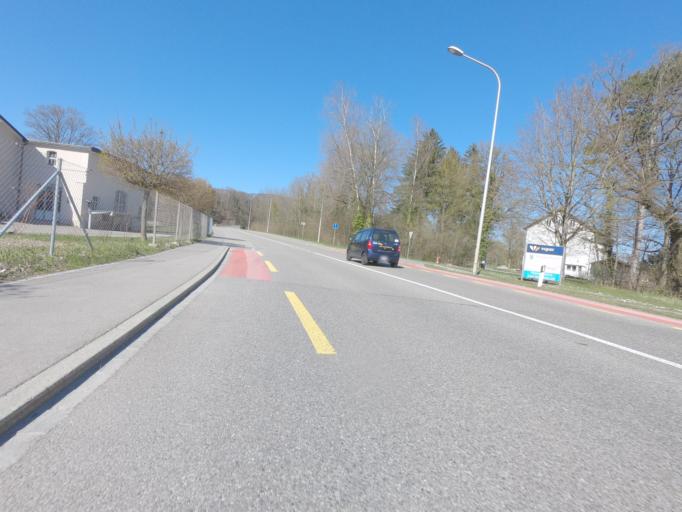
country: CH
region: Solothurn
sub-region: Bezirk Wasseramt
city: Luterbach
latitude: 47.2262
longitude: 7.5873
